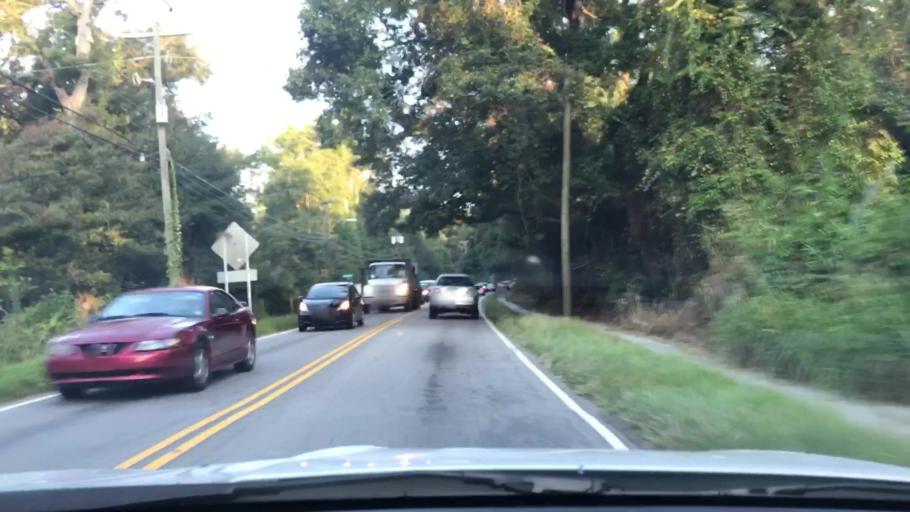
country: US
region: South Carolina
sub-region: Charleston County
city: North Charleston
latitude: 32.8124
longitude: -80.0294
